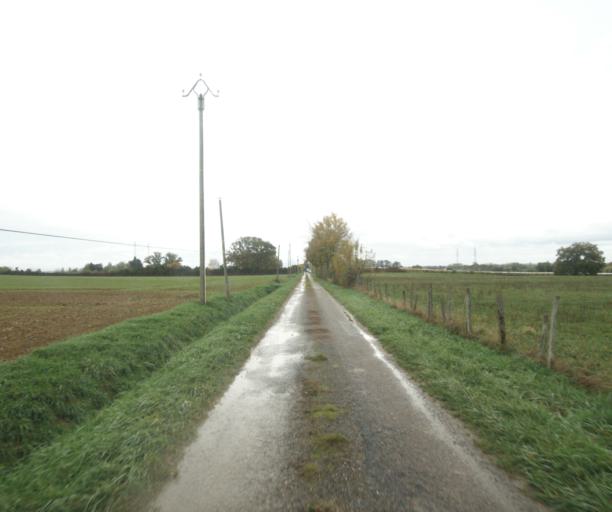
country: FR
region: Rhone-Alpes
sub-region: Departement de l'Ain
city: Pont-de-Vaux
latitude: 46.4845
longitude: 4.8821
